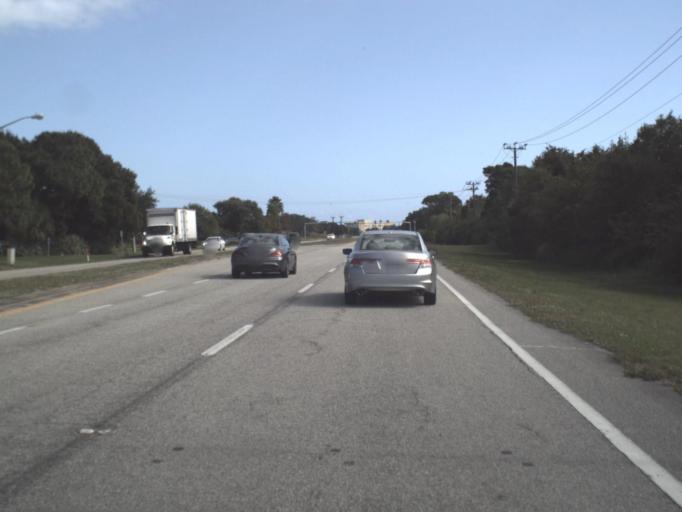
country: US
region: Florida
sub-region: Brevard County
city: West Melbourne
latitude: 28.0926
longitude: -80.6444
